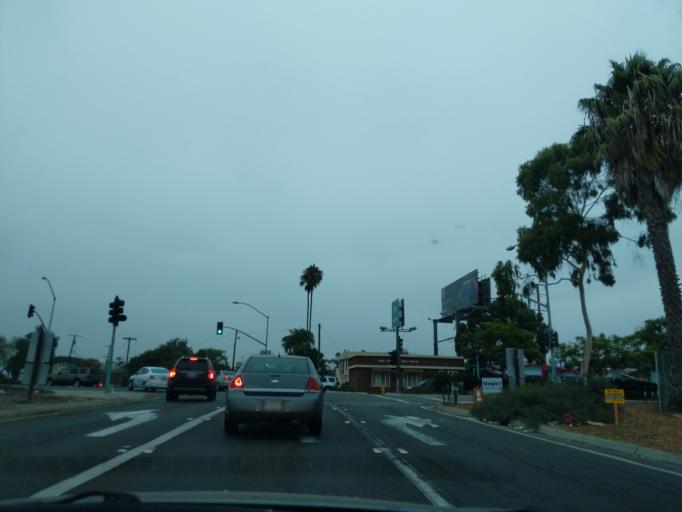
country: US
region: California
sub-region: San Diego County
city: San Diego
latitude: 32.7549
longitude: -117.1241
